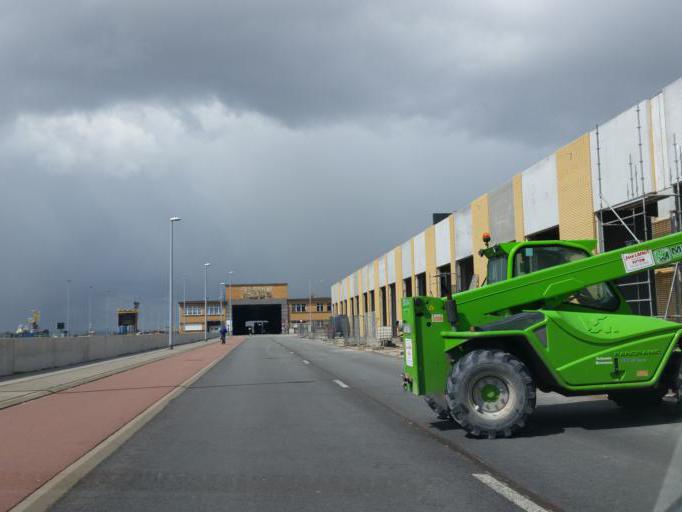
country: BE
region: Flanders
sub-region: Provincie West-Vlaanderen
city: Ostend
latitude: 51.2307
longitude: 2.9340
